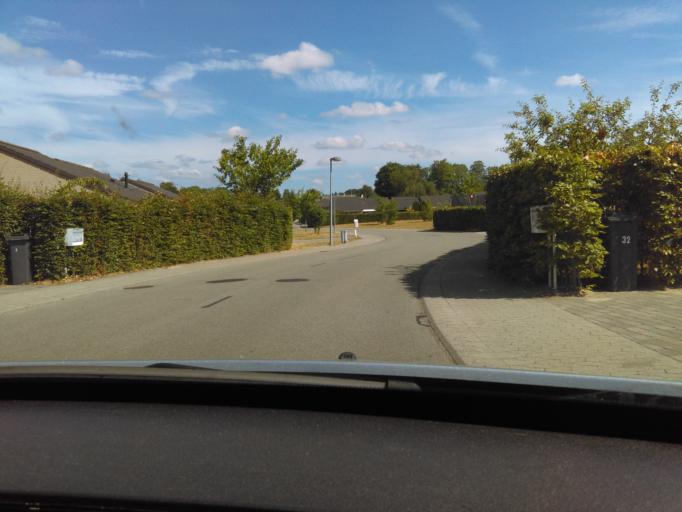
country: DK
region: Capital Region
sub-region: Fureso Kommune
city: Farum
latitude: 55.8237
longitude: 12.3531
